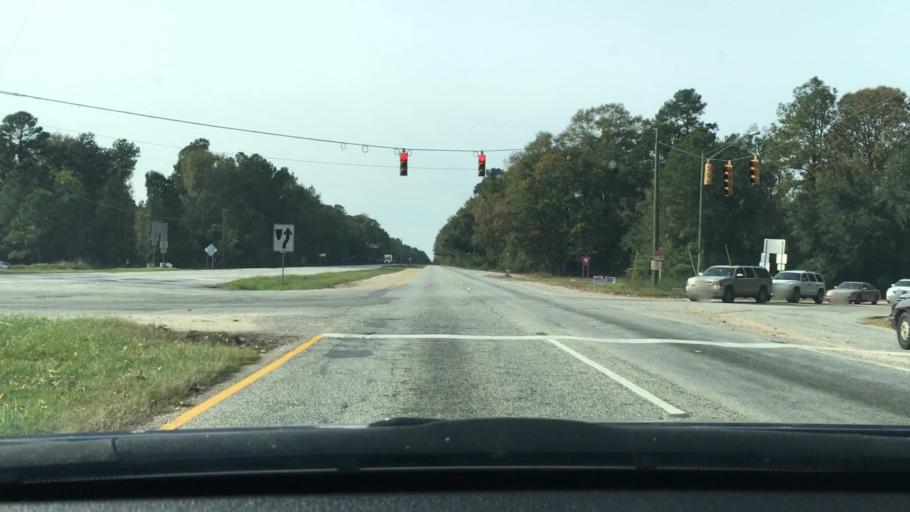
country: US
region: South Carolina
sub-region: Sumter County
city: Stateburg
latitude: 33.9455
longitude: -80.5240
